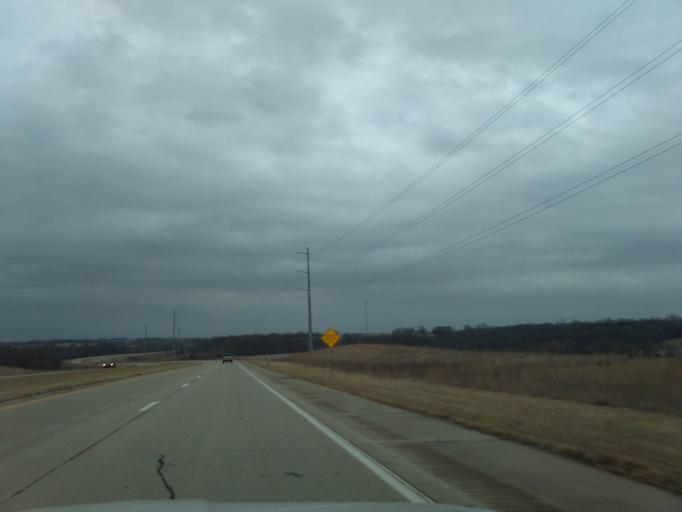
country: US
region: Nebraska
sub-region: Otoe County
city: Syracuse
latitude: 40.6755
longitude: -96.0467
